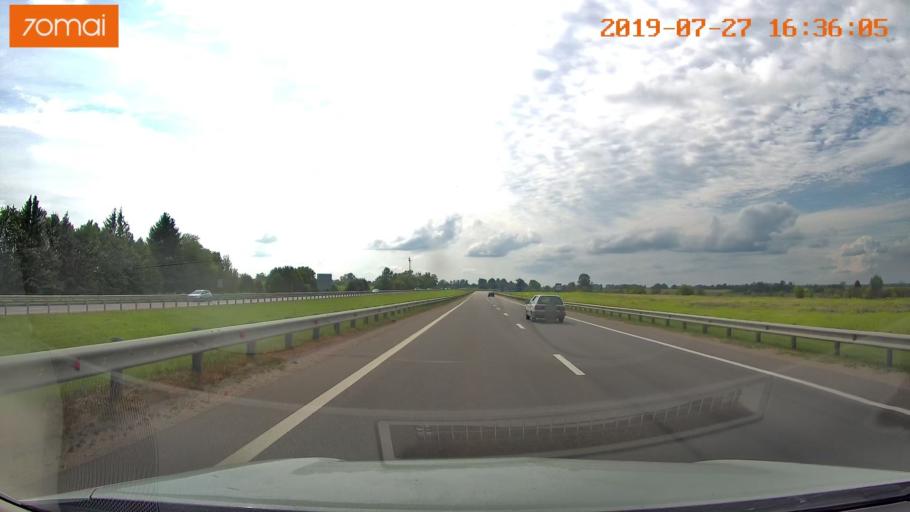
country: RU
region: Kaliningrad
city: Gvardeysk
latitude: 54.6487
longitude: 21.2930
